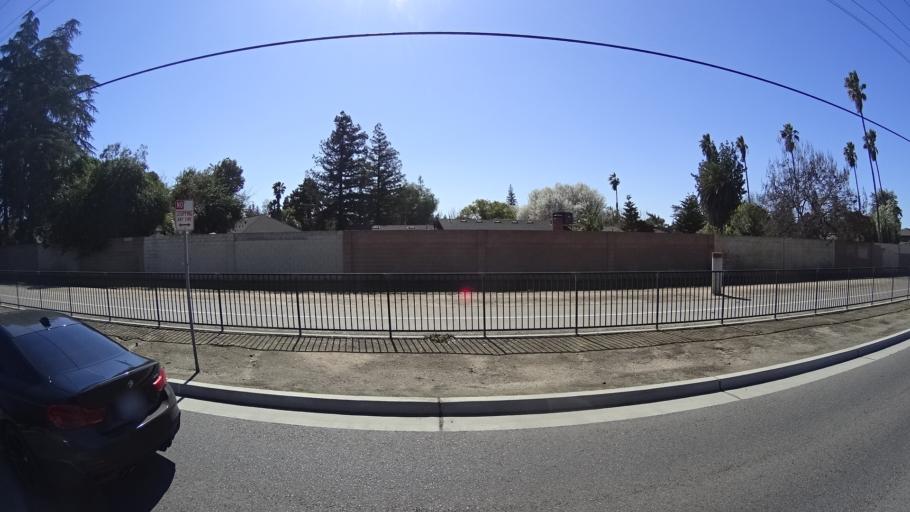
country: US
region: California
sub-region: Fresno County
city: Fresno
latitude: 36.8367
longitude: -119.8510
